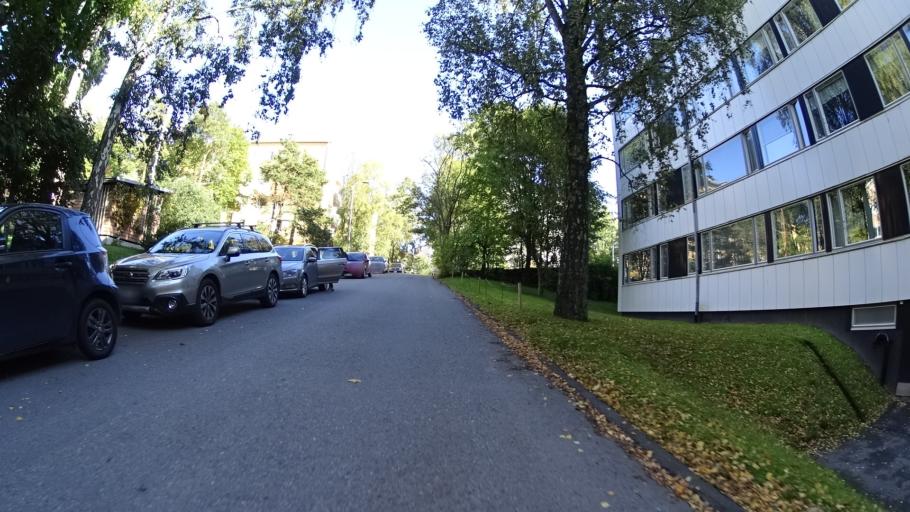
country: FI
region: Uusimaa
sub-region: Helsinki
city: Teekkarikylae
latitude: 60.1615
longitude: 24.8784
